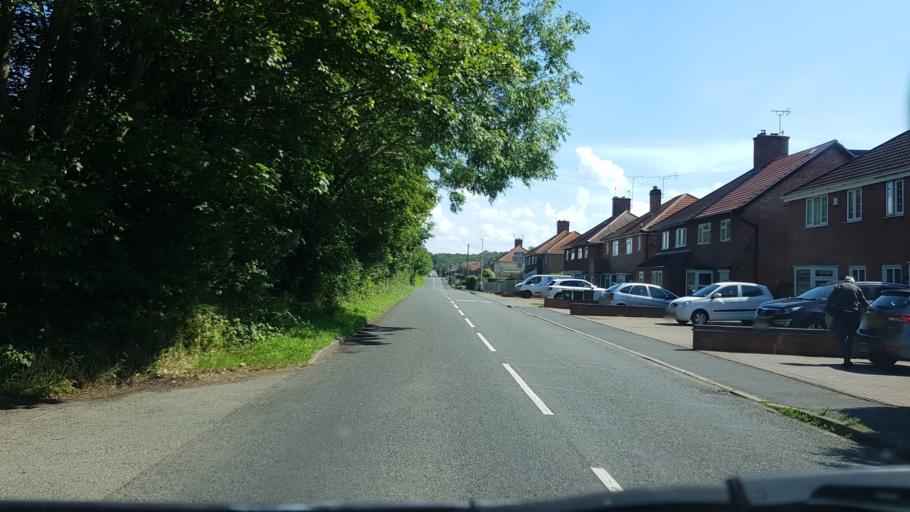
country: GB
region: England
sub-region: Worcestershire
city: Stourport-on-Severn
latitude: 52.3510
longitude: -2.2977
